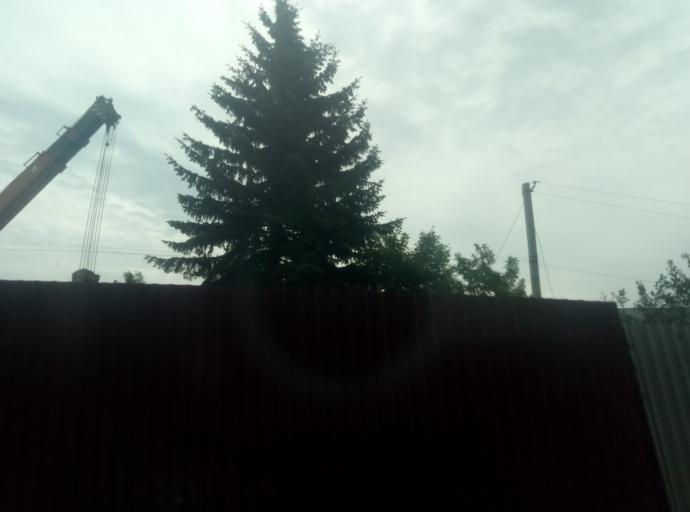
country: RU
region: Tula
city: Bogoroditsk
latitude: 53.7704
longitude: 38.1461
